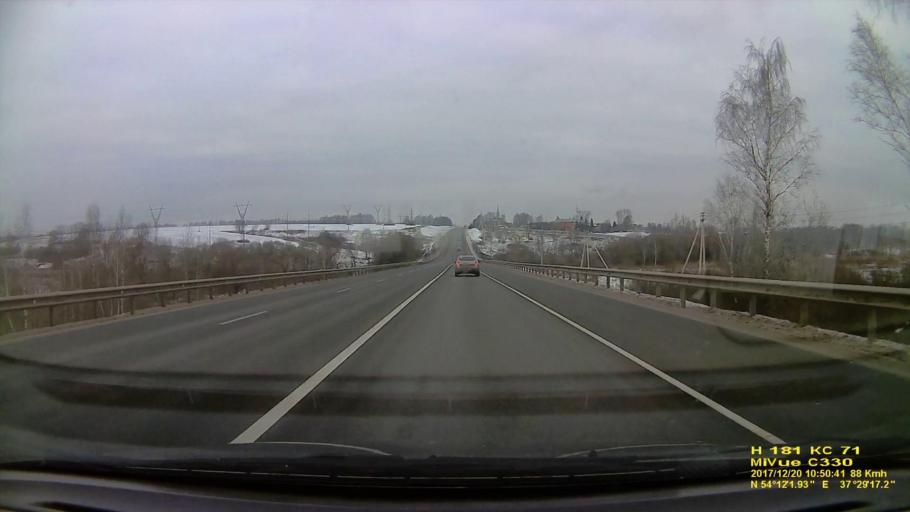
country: RU
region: Tula
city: Barsuki
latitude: 54.2007
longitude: 37.4881
